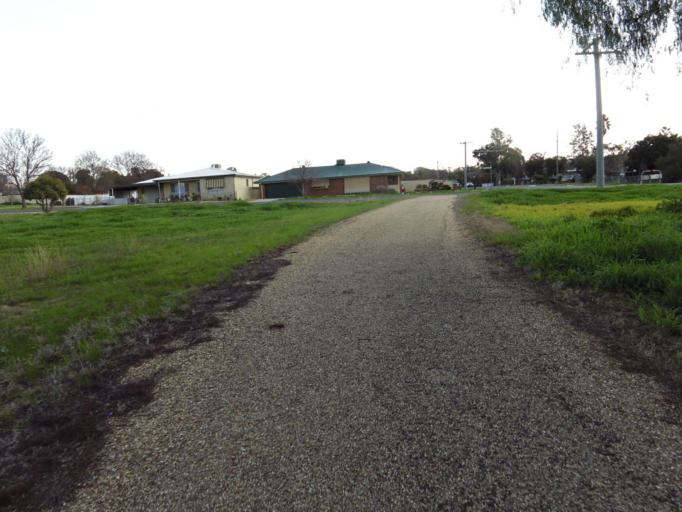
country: AU
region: New South Wales
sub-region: Corowa Shire
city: Corowa
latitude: -36.0113
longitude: 146.3992
